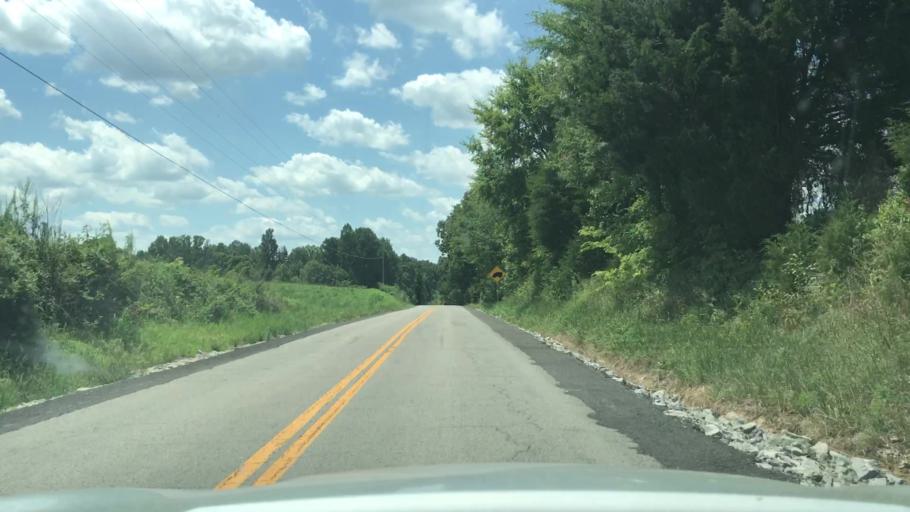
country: US
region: Kentucky
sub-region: Muhlenberg County
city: Greenville
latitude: 37.1272
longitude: -87.3011
